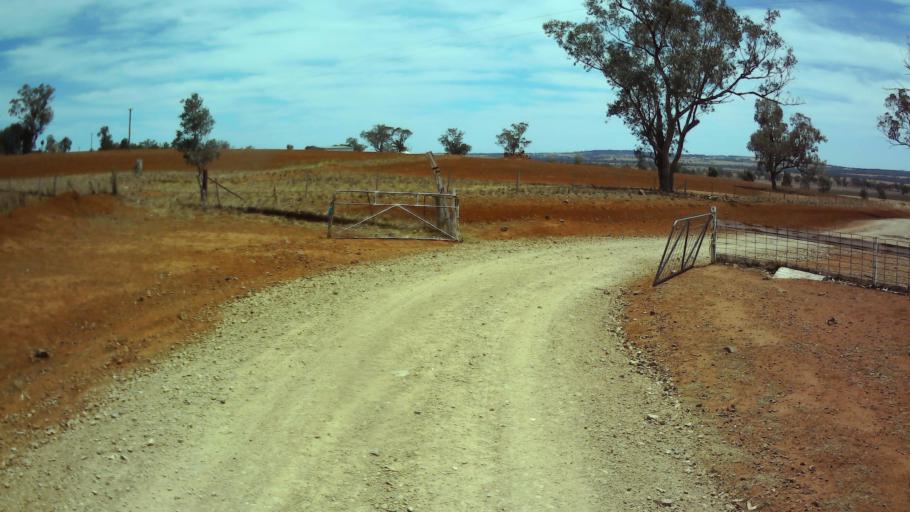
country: AU
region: New South Wales
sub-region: Weddin
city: Grenfell
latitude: -33.7501
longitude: 148.1555
